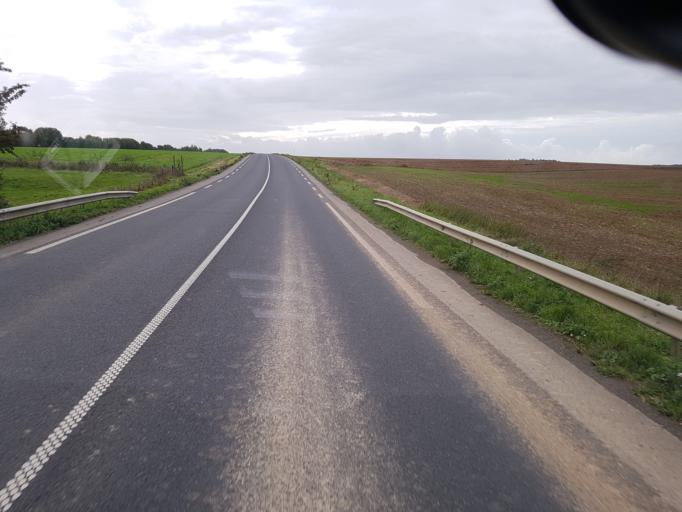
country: FR
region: Nord-Pas-de-Calais
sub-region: Departement du Pas-de-Calais
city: Avesnes-le-Comte
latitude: 50.1871
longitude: 2.4842
